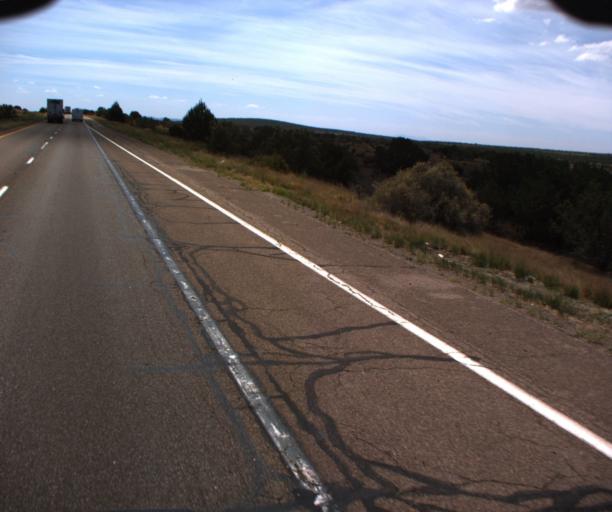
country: US
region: Arizona
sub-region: Yavapai County
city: Paulden
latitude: 35.2663
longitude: -112.7255
